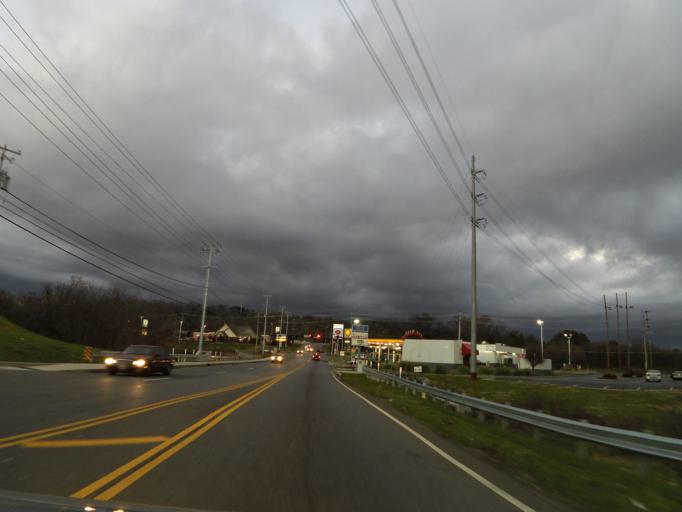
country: US
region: Tennessee
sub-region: Knox County
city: Knoxville
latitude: 36.0329
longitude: -83.8699
